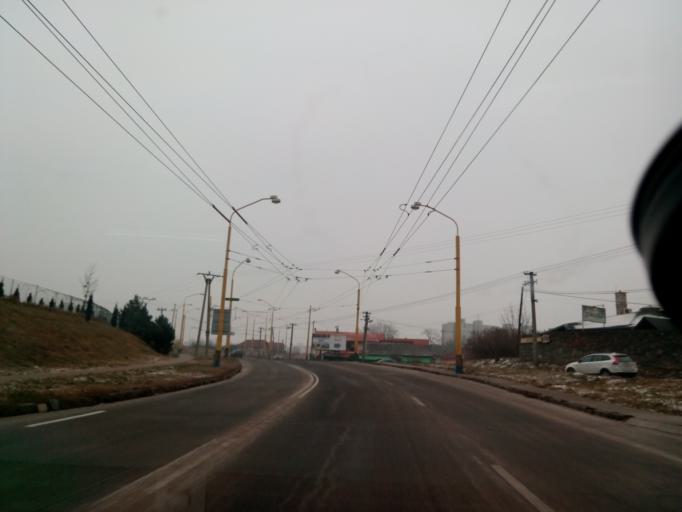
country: SK
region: Kosicky
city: Kosice
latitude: 48.7097
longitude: 21.2056
